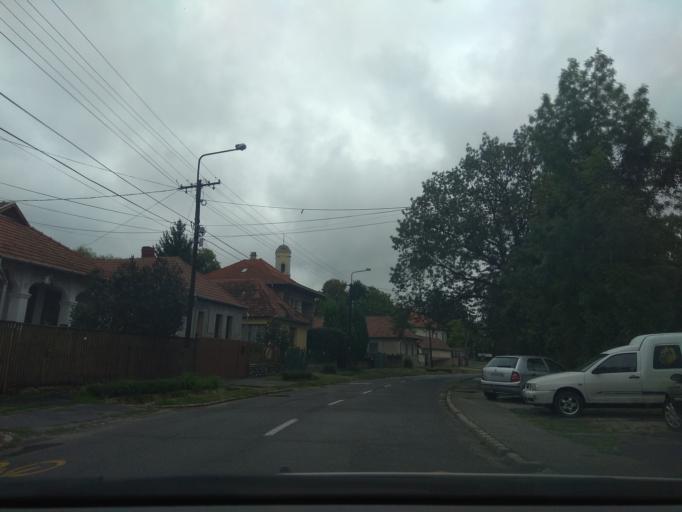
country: HU
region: Borsod-Abauj-Zemplen
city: Miskolc
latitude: 48.0565
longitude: 20.7823
